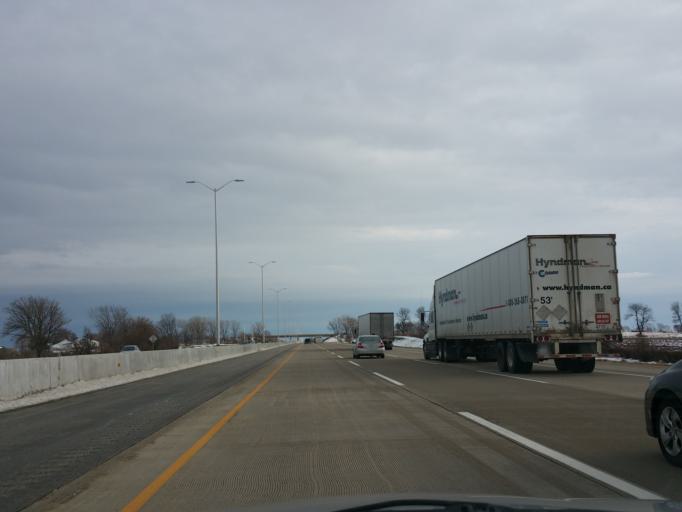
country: US
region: Illinois
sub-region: Boone County
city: Belvidere
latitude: 42.2282
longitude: -88.7716
